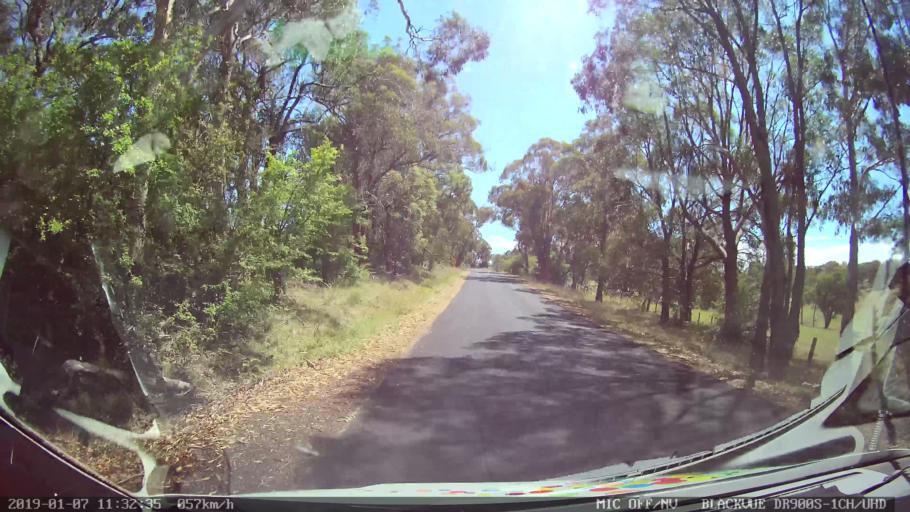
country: AU
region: New South Wales
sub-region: Armidale Dumaresq
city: Armidale
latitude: -30.4081
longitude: 151.5595
